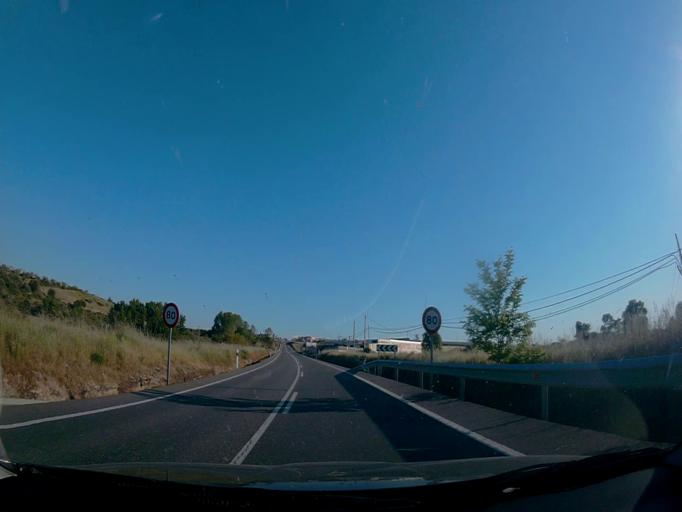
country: ES
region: Castille-La Mancha
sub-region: Province of Toledo
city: Escalona
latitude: 40.1538
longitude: -4.4024
